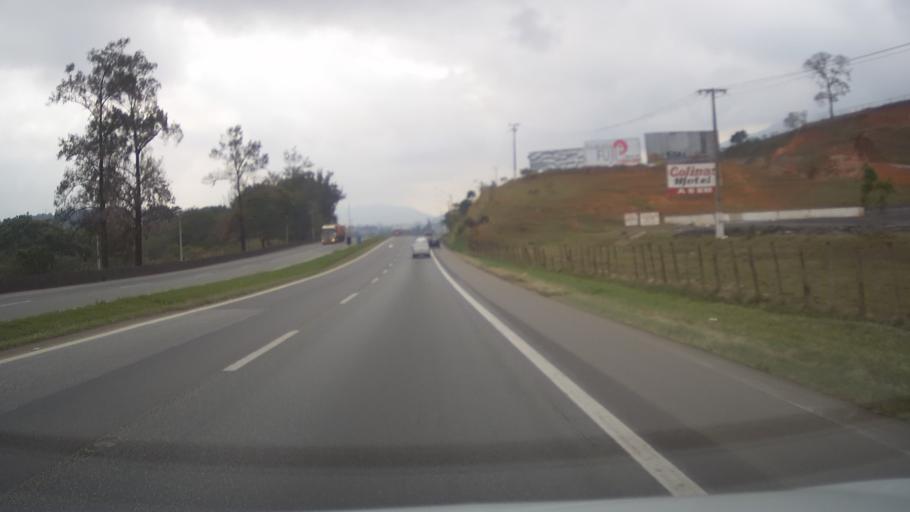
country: BR
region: Minas Gerais
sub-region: Extrema
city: Extrema
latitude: -22.8664
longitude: -46.3499
